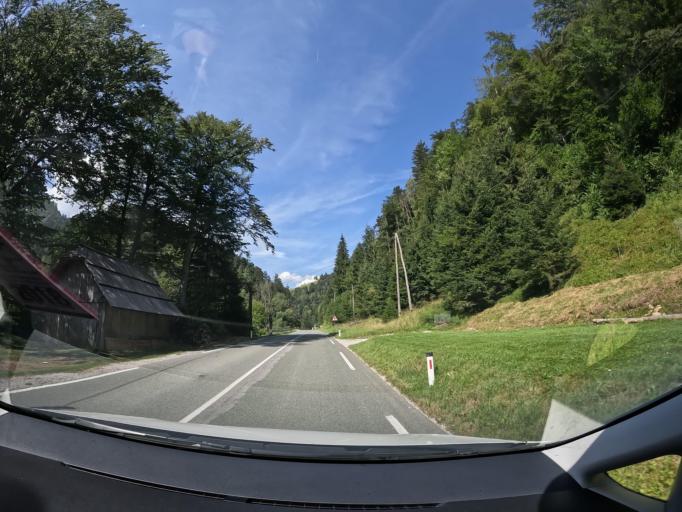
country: SI
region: Preddvor
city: Preddvor
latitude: 46.3671
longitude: 14.4179
